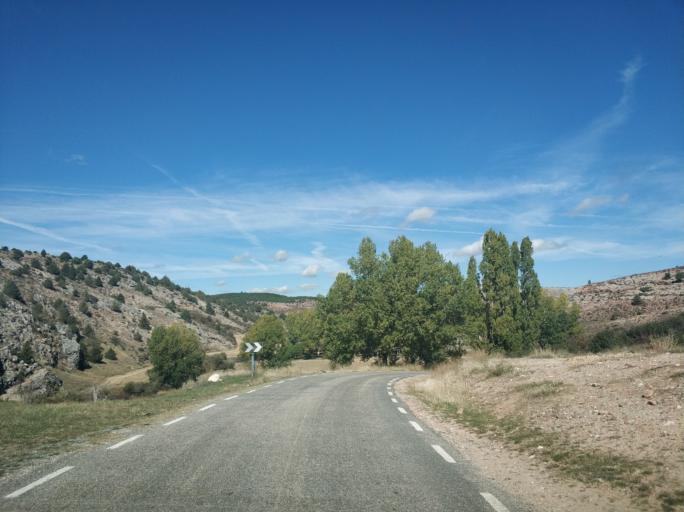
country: ES
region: Castille and Leon
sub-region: Provincia de Soria
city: Espeja de San Marcelino
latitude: 41.8049
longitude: -3.2240
